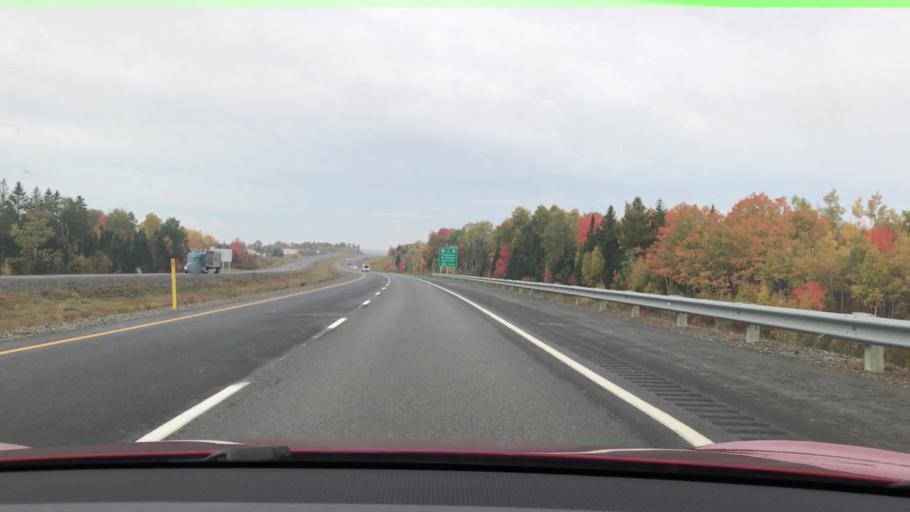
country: US
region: Maine
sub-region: Washington County
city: Calais
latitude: 45.2166
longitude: -67.2412
